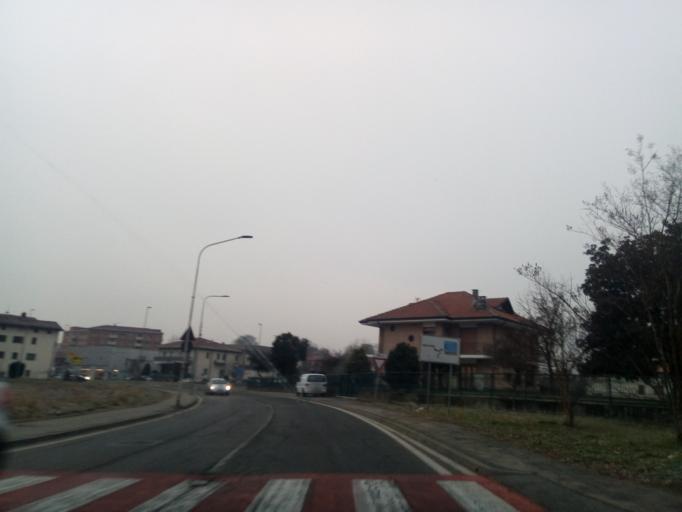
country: IT
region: Piedmont
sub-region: Provincia di Torino
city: Banchette
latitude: 45.4550
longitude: 7.8550
